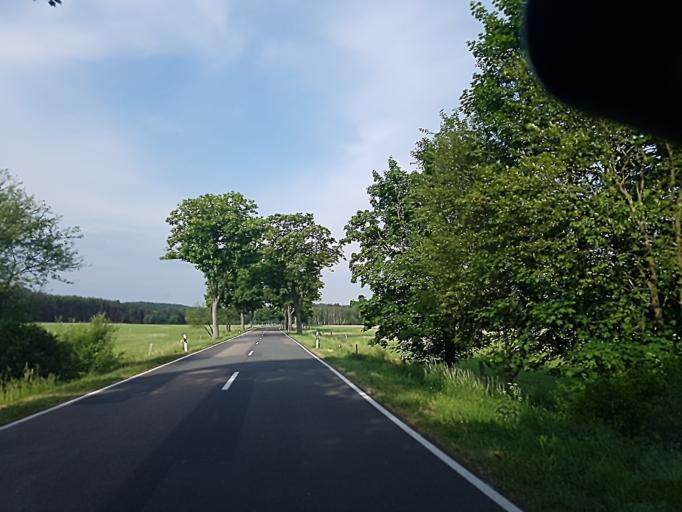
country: DE
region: Brandenburg
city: Niemegk
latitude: 52.0471
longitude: 12.6114
